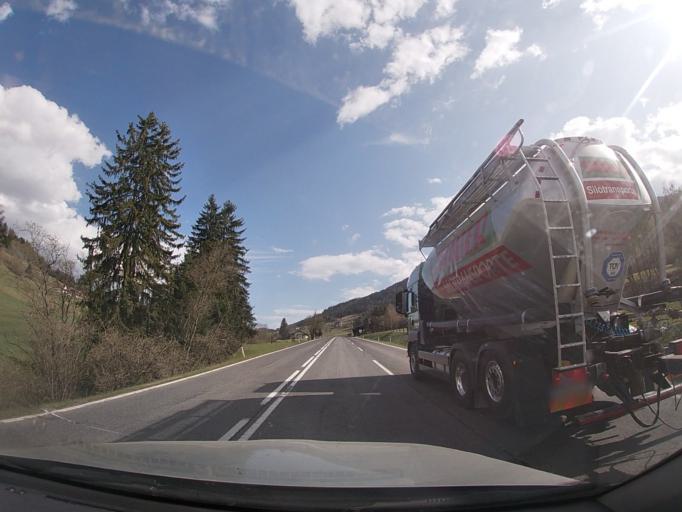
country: AT
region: Styria
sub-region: Politischer Bezirk Murau
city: Sankt Lorenzen bei Scheifling
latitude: 47.1330
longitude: 14.4354
